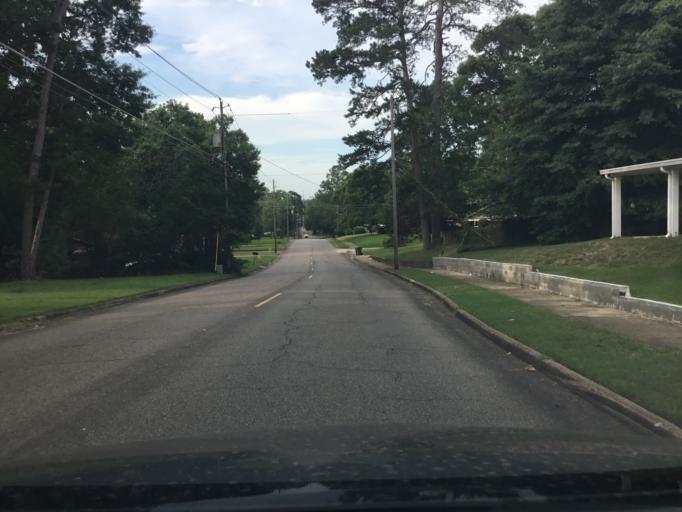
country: US
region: Alabama
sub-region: Montgomery County
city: Montgomery
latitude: 32.3710
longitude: -86.2555
